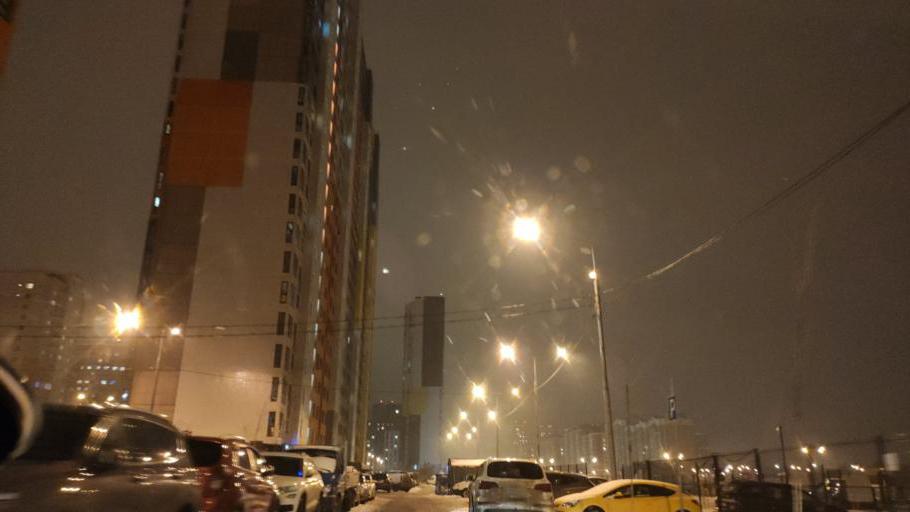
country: RU
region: Moskovskaya
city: Shcherbinka
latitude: 55.5246
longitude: 37.5981
